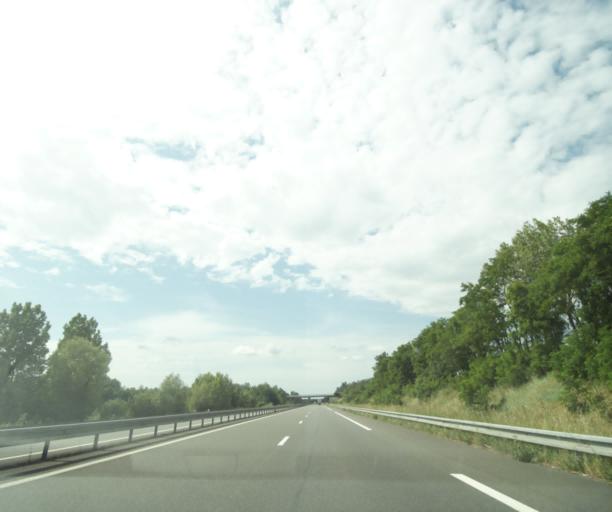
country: FR
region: Pays de la Loire
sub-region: Departement de Maine-et-Loire
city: Jumelles
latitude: 47.3948
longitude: -0.1114
